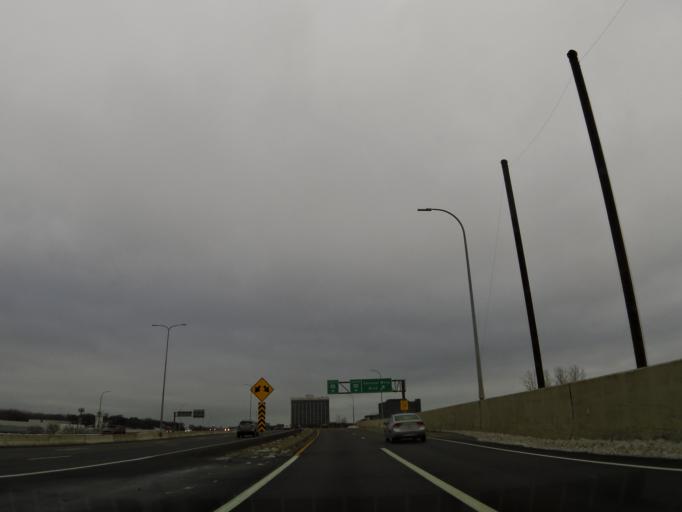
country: US
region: Minnesota
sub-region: Hennepin County
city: Saint Louis Park
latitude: 44.9741
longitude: -93.3886
